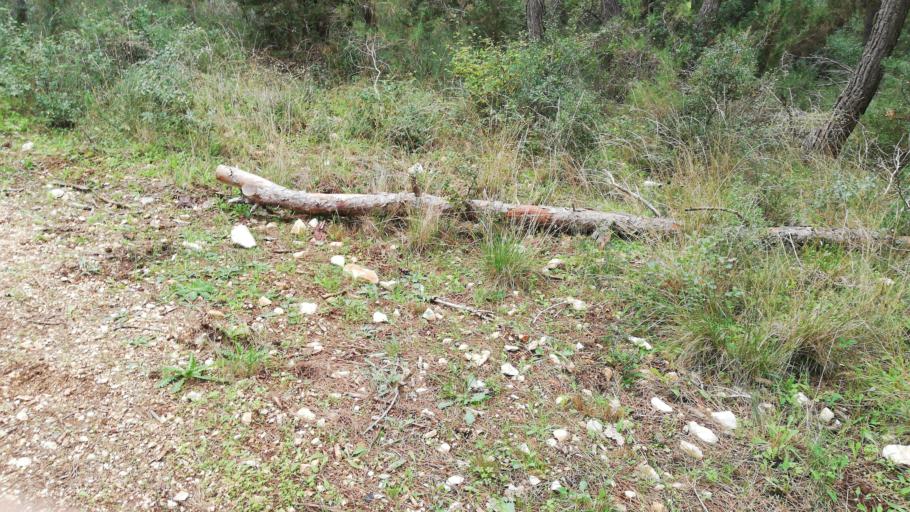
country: IT
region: Apulia
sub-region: Provincia di Bari
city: Cassano delle Murge
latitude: 40.8726
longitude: 16.7143
